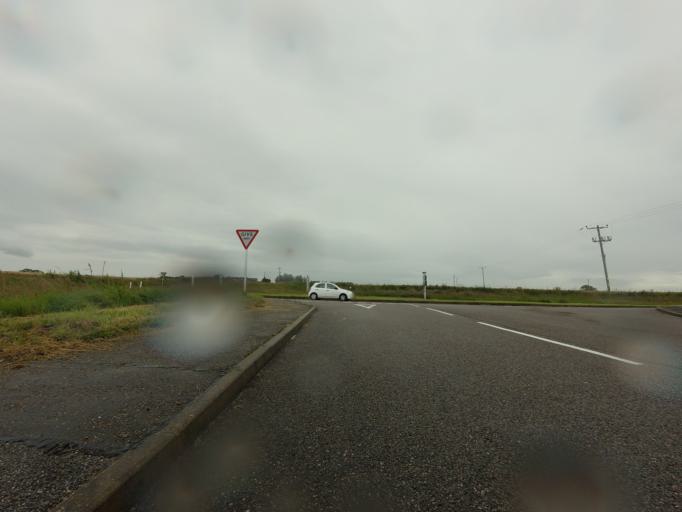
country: GB
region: Scotland
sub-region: Moray
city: Findochty
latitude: 57.6959
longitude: -2.8983
